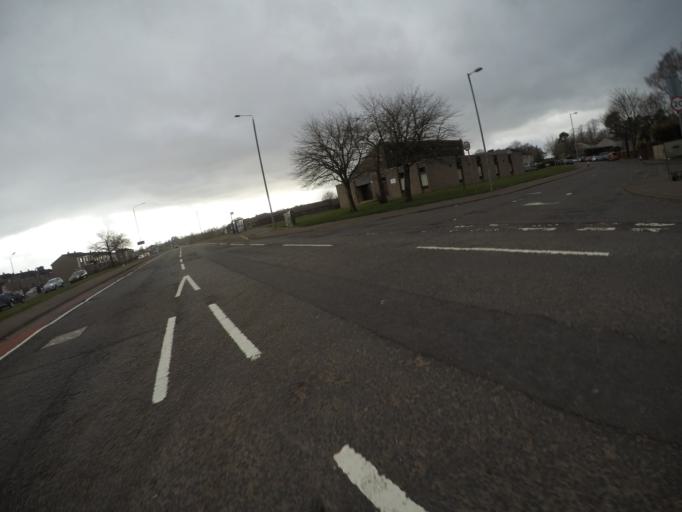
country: GB
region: Scotland
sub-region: East Ayrshire
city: Kilmarnock
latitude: 55.6185
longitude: -4.4770
